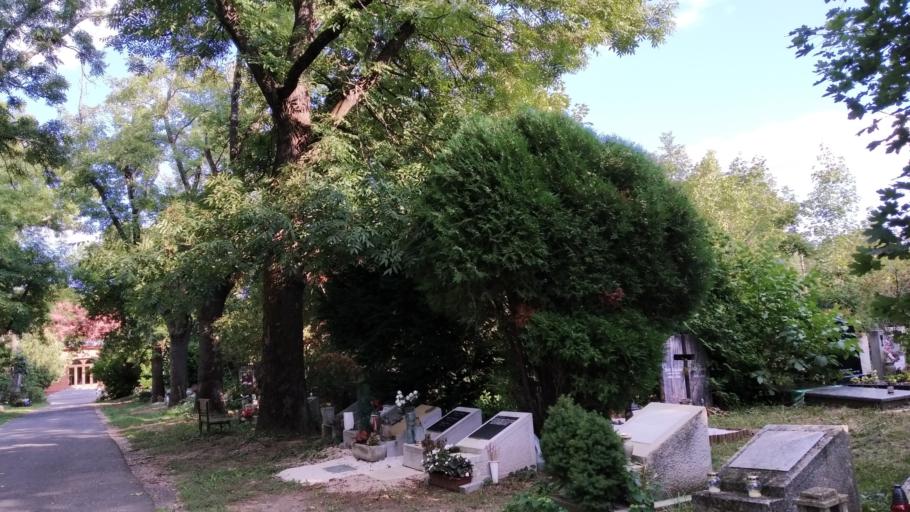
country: HU
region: Pest
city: Urom
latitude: 47.5691
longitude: 19.0238
